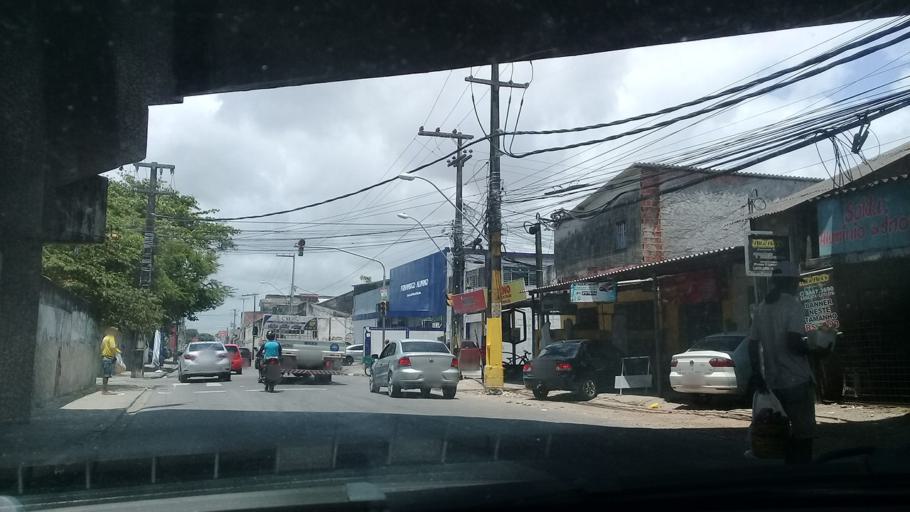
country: BR
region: Pernambuco
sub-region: Recife
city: Recife
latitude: -8.0774
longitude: -34.8989
